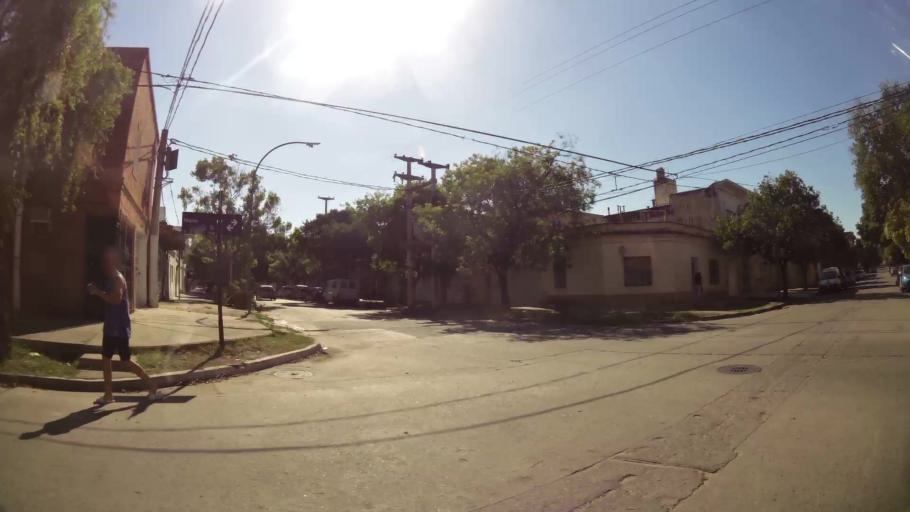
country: AR
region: Cordoba
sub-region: Departamento de Capital
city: Cordoba
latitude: -31.4128
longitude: -64.1584
